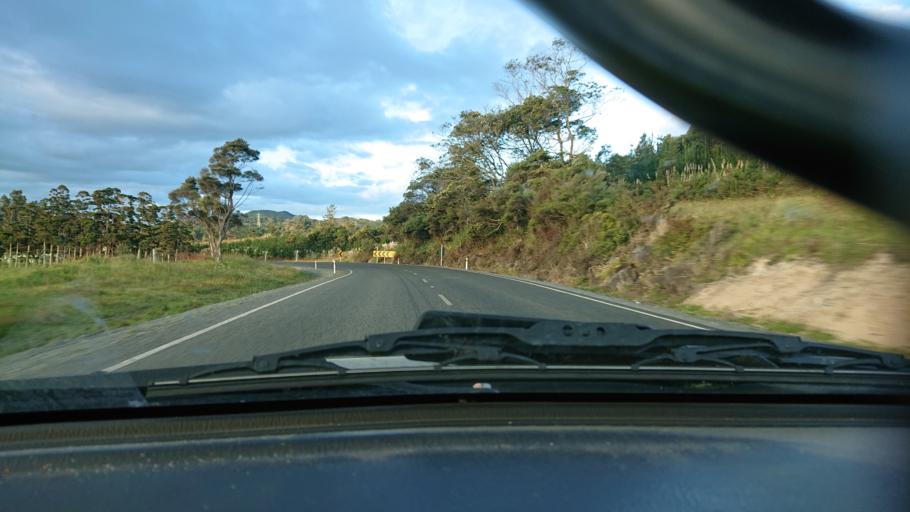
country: NZ
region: Auckland
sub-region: Auckland
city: Parakai
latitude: -36.5143
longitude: 174.4522
